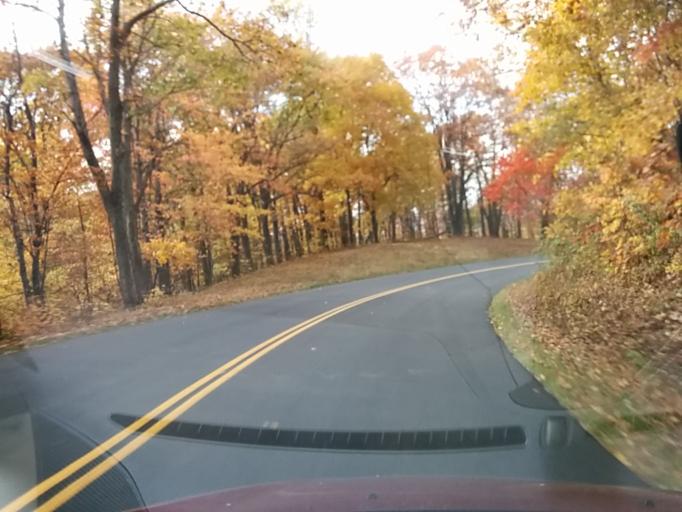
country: US
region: Virginia
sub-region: Augusta County
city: Stuarts Draft
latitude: 37.8869
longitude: -79.0202
